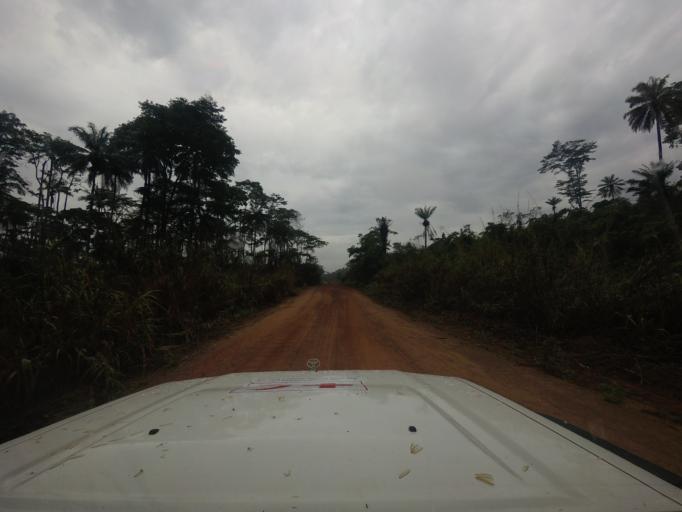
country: LR
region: Lofa
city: Voinjama
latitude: 8.3882
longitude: -9.8176
